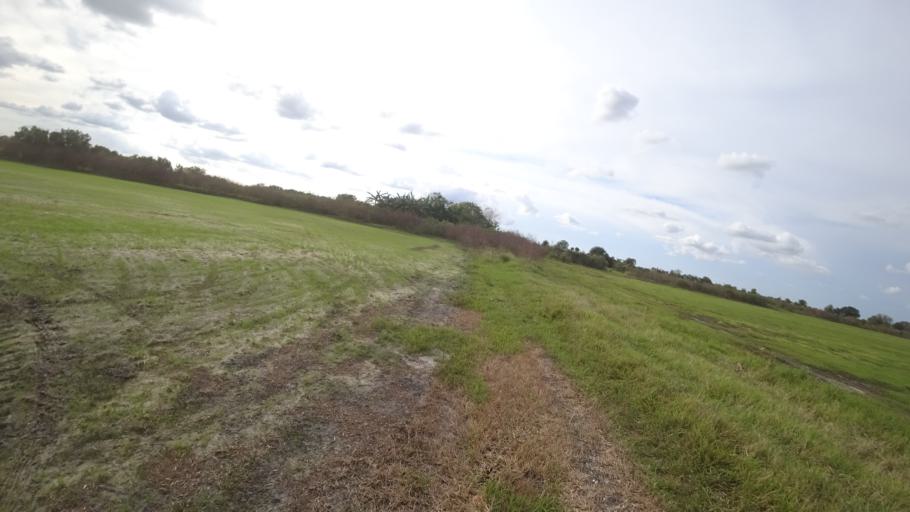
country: US
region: Florida
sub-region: Hardee County
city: Wauchula
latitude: 27.5276
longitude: -82.0856
